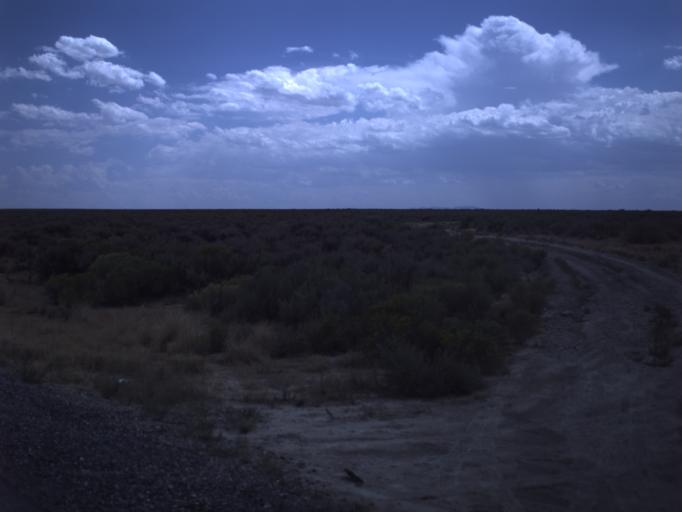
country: US
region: Utah
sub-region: Tooele County
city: Tooele
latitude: 40.3798
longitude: -112.3836
